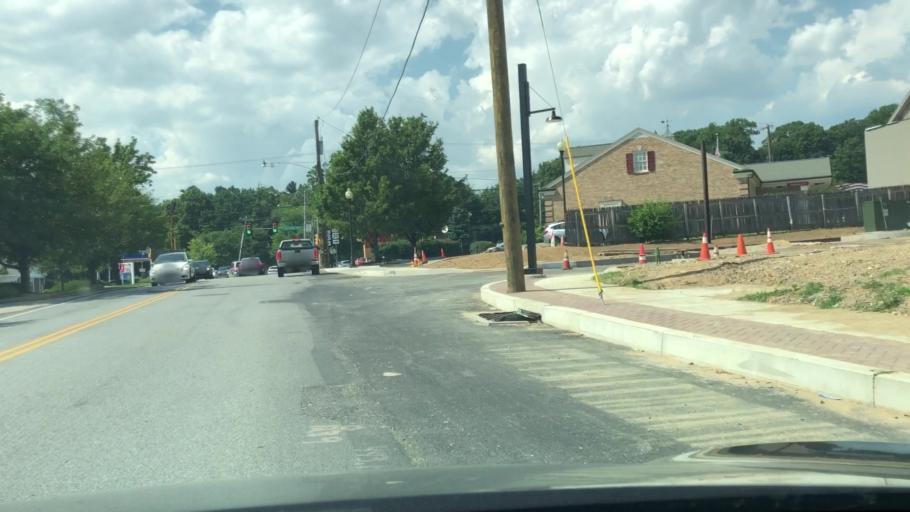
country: US
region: Pennsylvania
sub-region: Chester County
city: Devon
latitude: 40.0451
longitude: -75.4229
